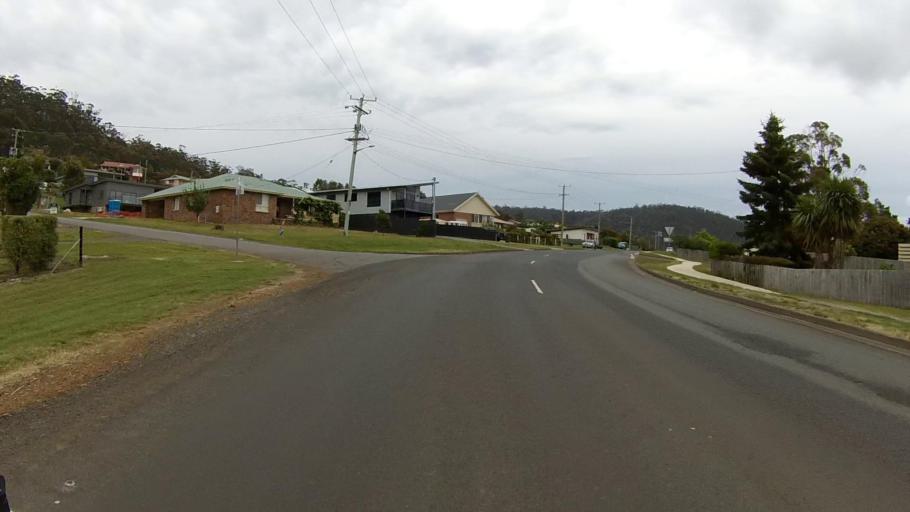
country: AU
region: Tasmania
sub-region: Sorell
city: Sorell
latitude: -42.5665
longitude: 147.8740
